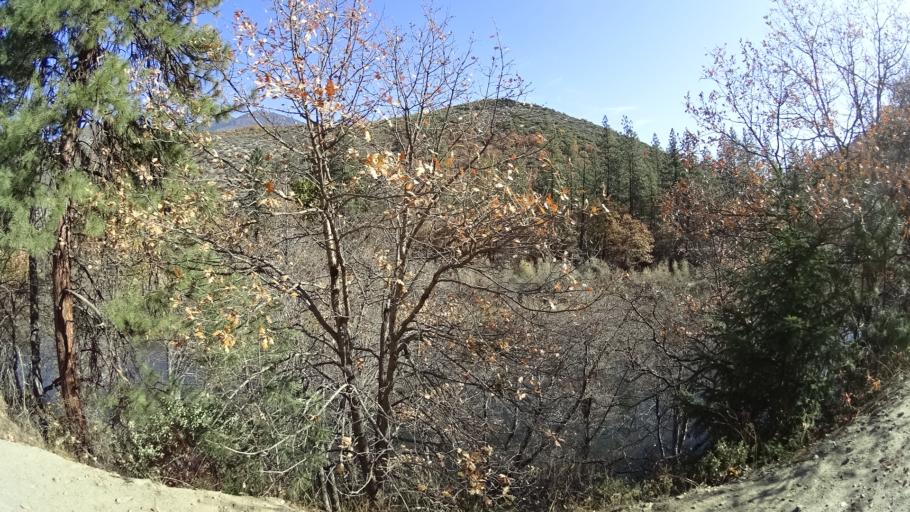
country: US
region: California
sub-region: Siskiyou County
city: Yreka
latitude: 41.8582
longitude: -122.7056
